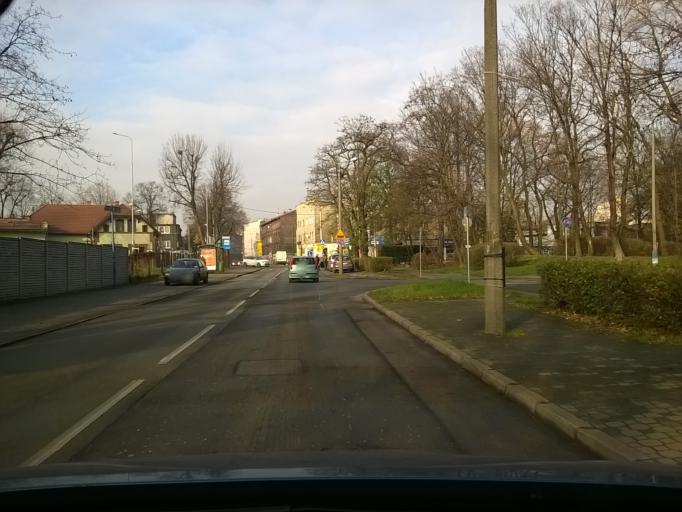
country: PL
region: Silesian Voivodeship
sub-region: Chorzow
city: Chorzow
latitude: 50.2850
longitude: 18.9509
